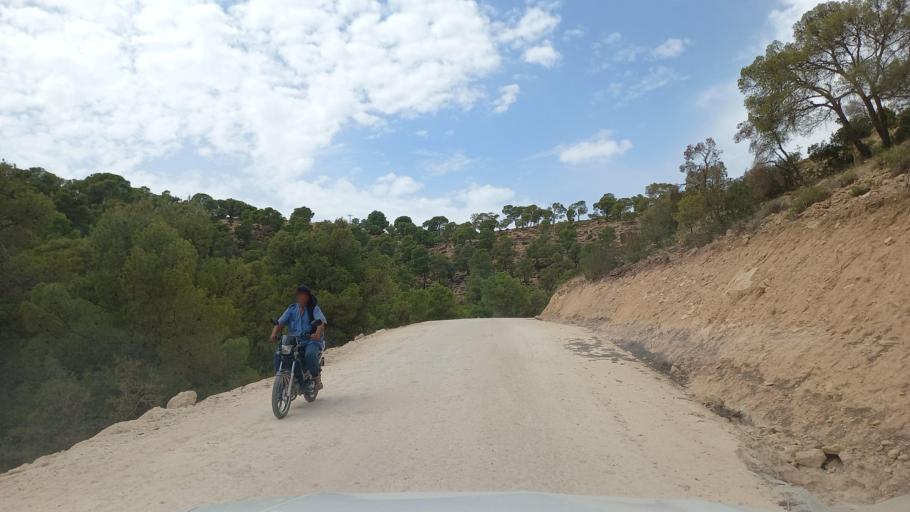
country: TN
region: Al Qasrayn
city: Kasserine
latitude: 35.3779
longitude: 8.8830
